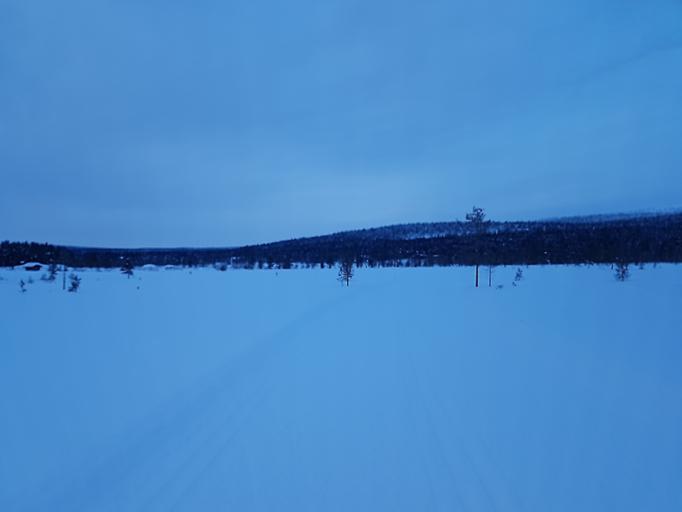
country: FI
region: Lapland
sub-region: Tunturi-Lappi
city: Kolari
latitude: 67.6196
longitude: 24.1333
